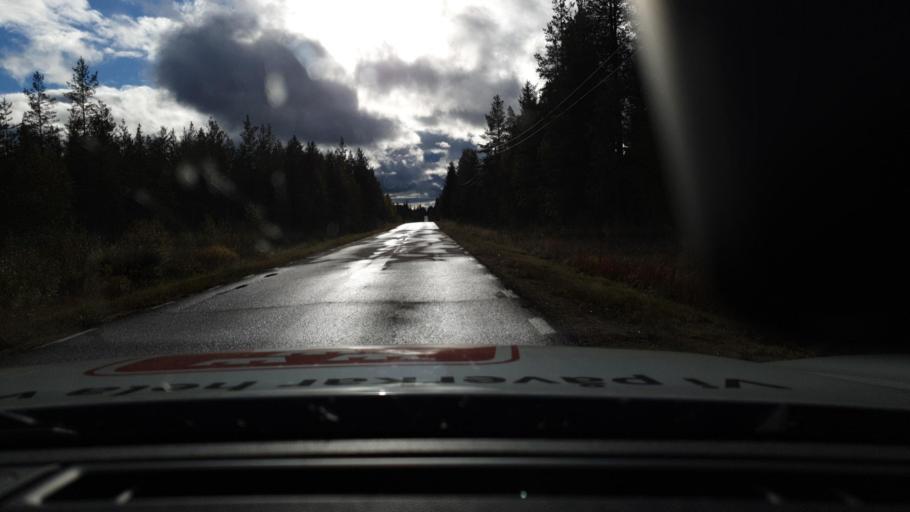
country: SE
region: Norrbotten
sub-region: Overkalix Kommun
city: OEverkalix
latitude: 67.0080
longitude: 22.5270
